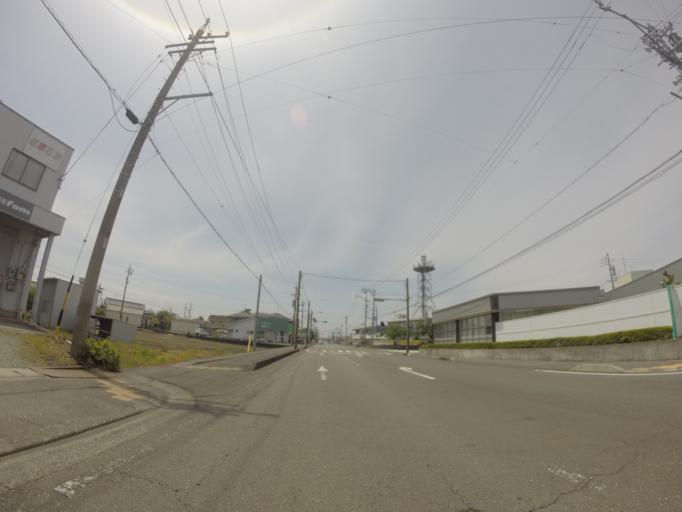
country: JP
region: Shizuoka
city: Yaizu
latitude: 34.8360
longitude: 138.3083
